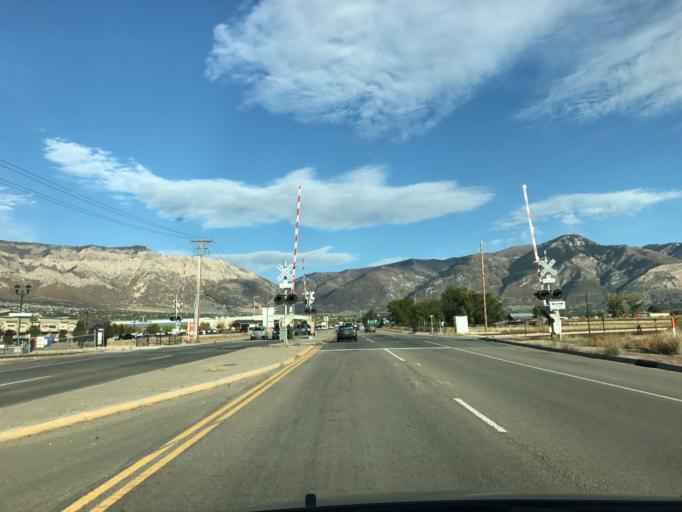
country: US
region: Utah
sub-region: Weber County
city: Farr West
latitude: 41.3068
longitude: -112.0108
